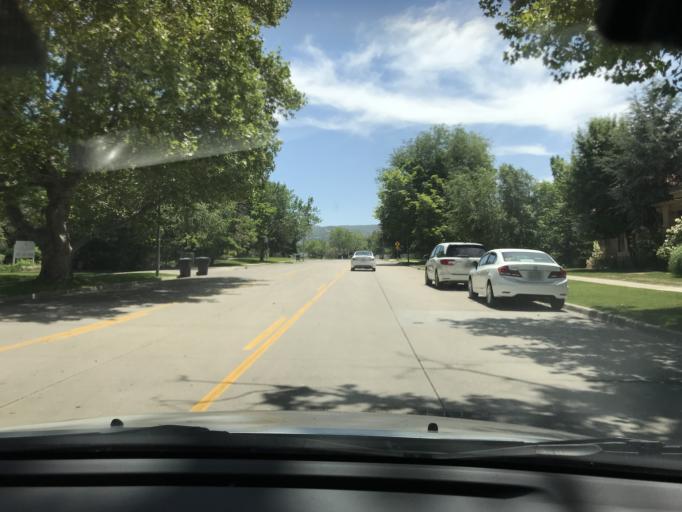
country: US
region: Utah
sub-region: Davis County
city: Bountiful
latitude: 40.8828
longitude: -111.8807
